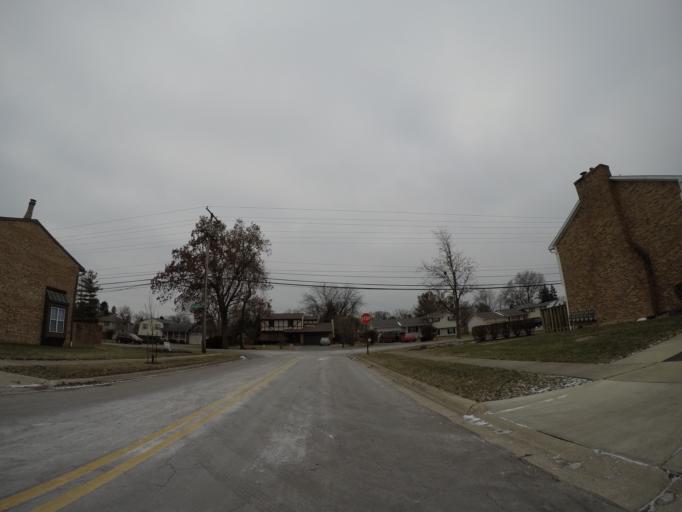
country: US
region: Ohio
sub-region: Franklin County
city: Worthington
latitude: 40.0521
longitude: -83.0579
